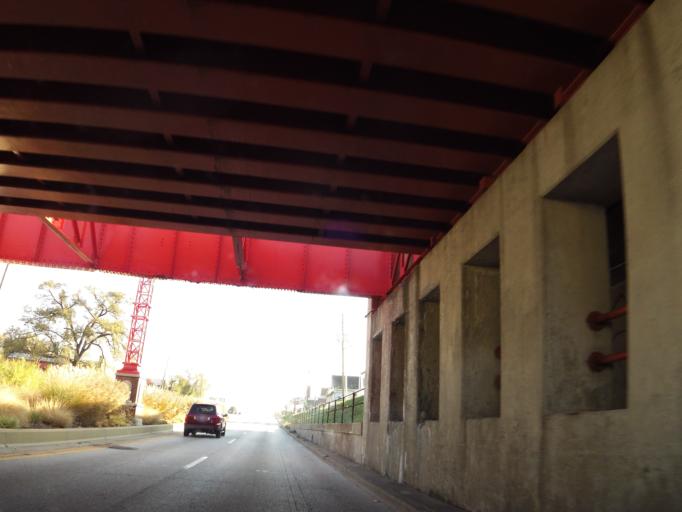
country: US
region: Indiana
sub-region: Marion County
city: Speedway
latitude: 39.7876
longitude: -86.2256
